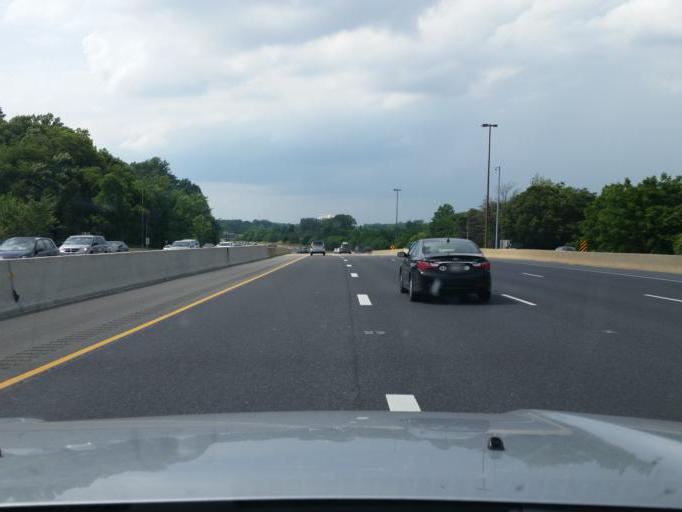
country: US
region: Maryland
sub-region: Montgomery County
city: Gaithersburg
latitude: 39.1480
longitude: -77.2162
